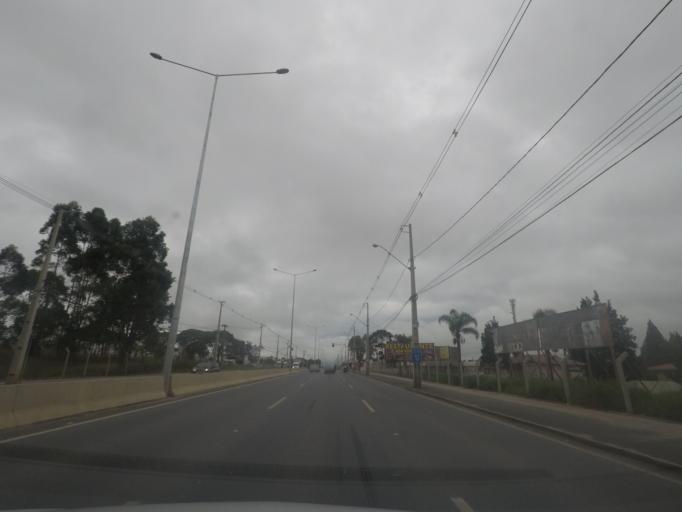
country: BR
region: Parana
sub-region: Piraquara
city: Piraquara
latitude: -25.4588
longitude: -49.0985
